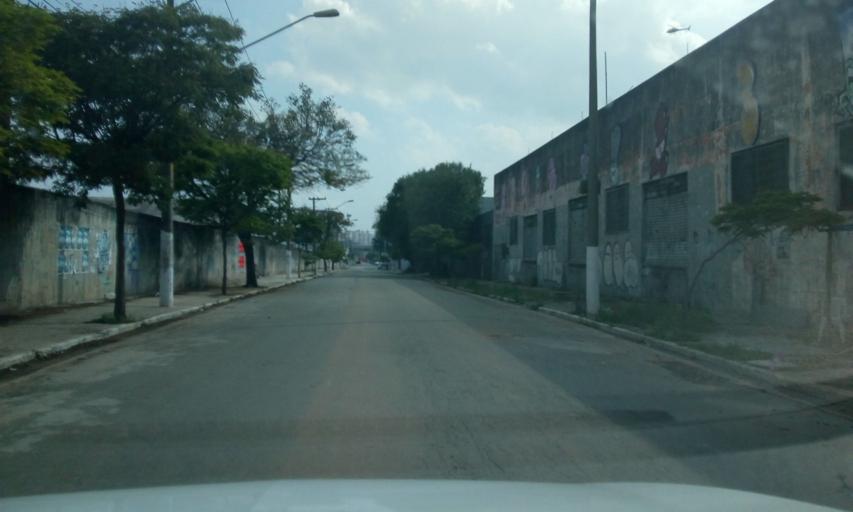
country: BR
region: Sao Paulo
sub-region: Osasco
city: Osasco
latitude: -23.5324
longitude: -46.7388
